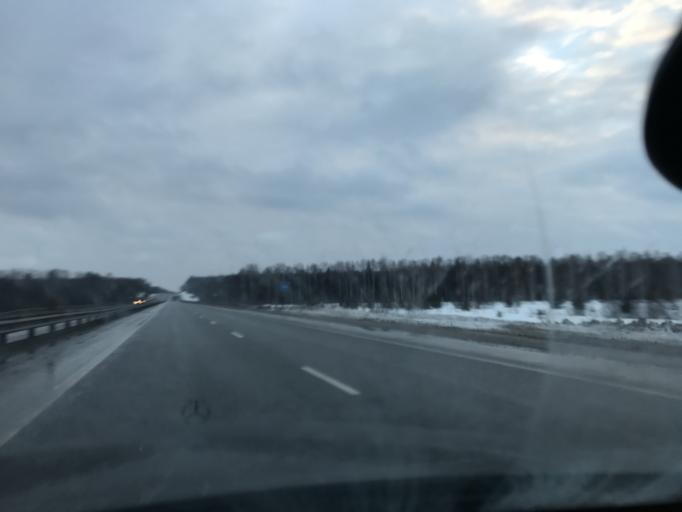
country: RU
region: Vladimir
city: Sudogda
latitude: 56.1260
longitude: 40.8677
